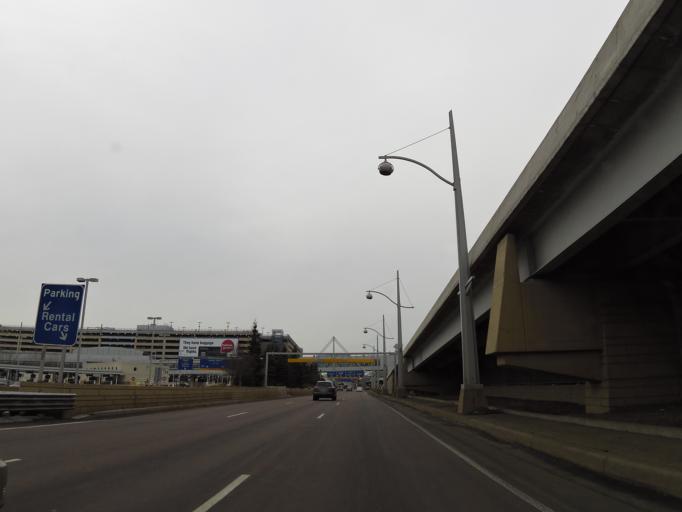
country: US
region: Minnesota
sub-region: Dakota County
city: Mendota Heights
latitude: 44.8808
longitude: -93.2019
